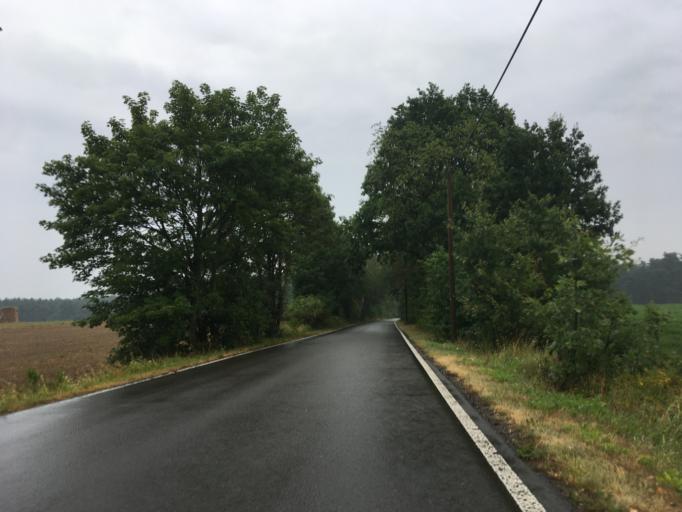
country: DE
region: Brandenburg
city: Marienwerder
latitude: 52.9075
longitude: 13.5613
